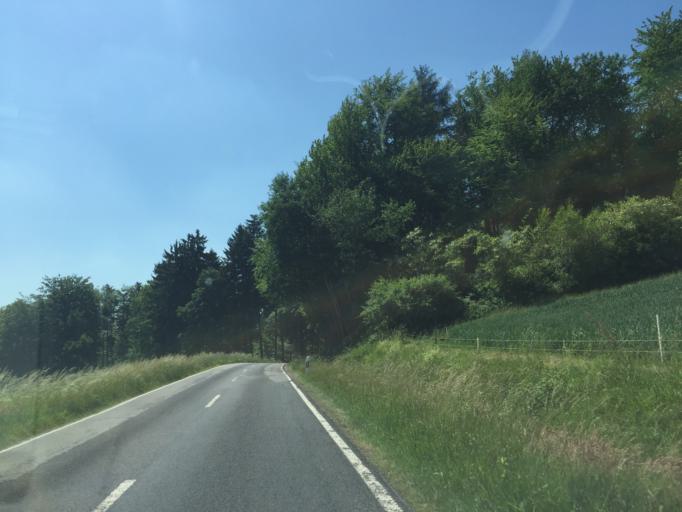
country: DE
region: Bavaria
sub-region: Regierungsbezirk Unterfranken
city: Eichenbuhl
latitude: 49.6555
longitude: 9.3079
